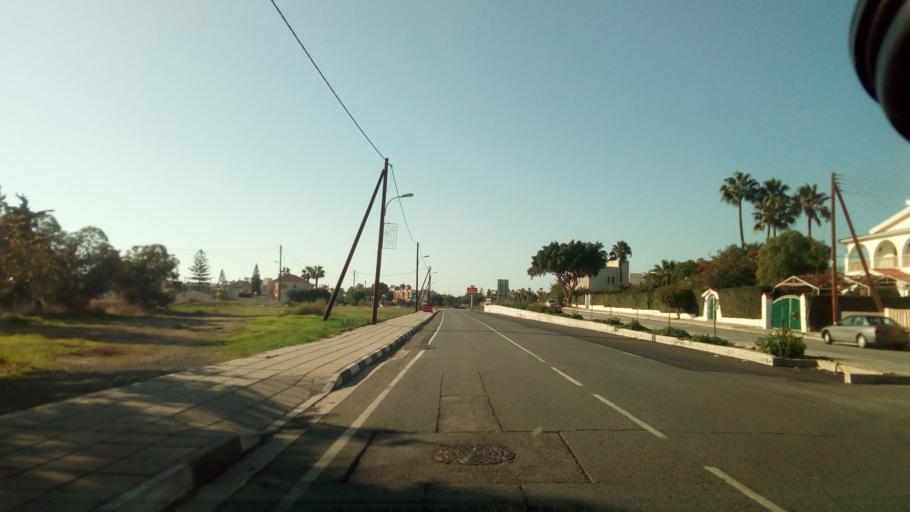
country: CY
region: Larnaka
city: Voroklini
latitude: 34.9767
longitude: 33.6743
